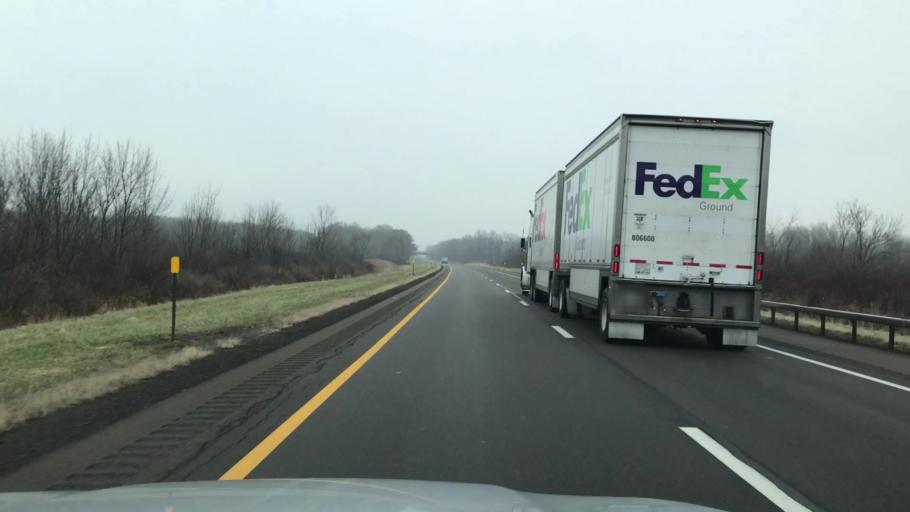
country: US
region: New York
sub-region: Chautauqua County
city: Westfield
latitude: 42.3589
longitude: -79.5303
